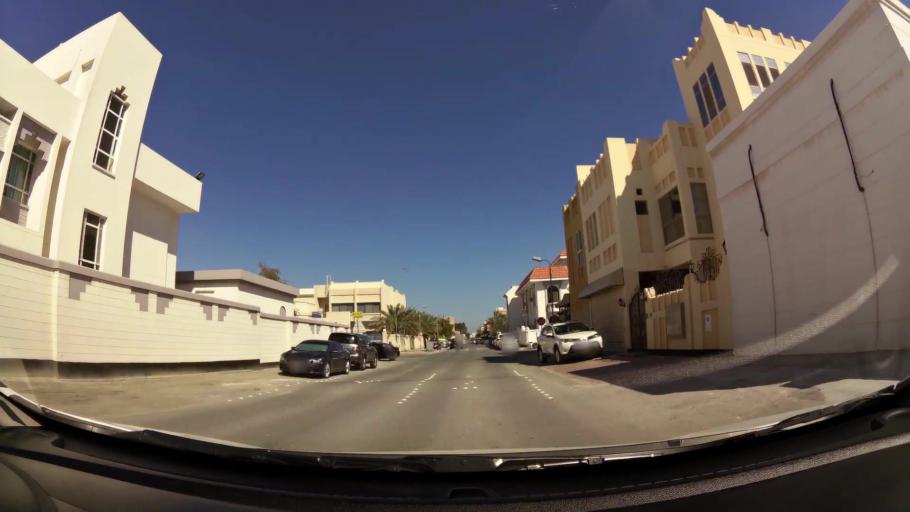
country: BH
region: Muharraq
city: Al Hadd
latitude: 26.2535
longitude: 50.6428
